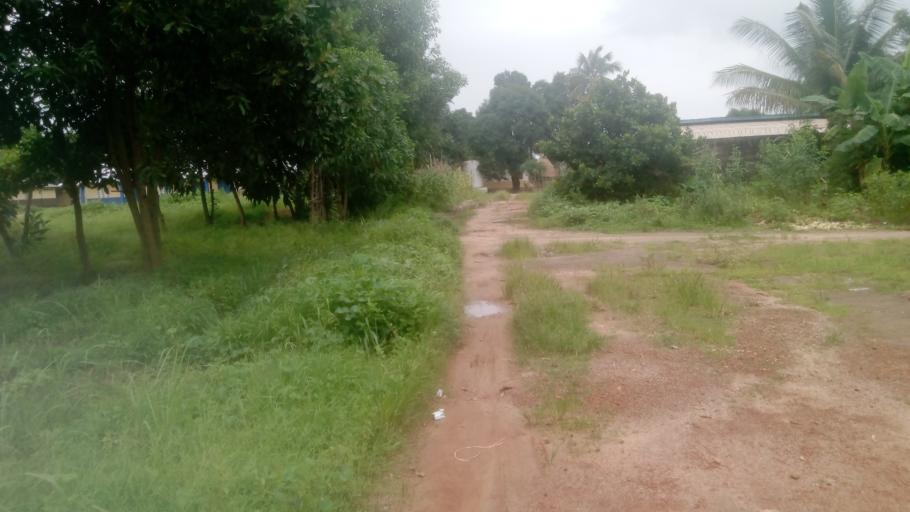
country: SL
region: Northern Province
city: Lunsar
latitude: 8.6845
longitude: -12.5462
